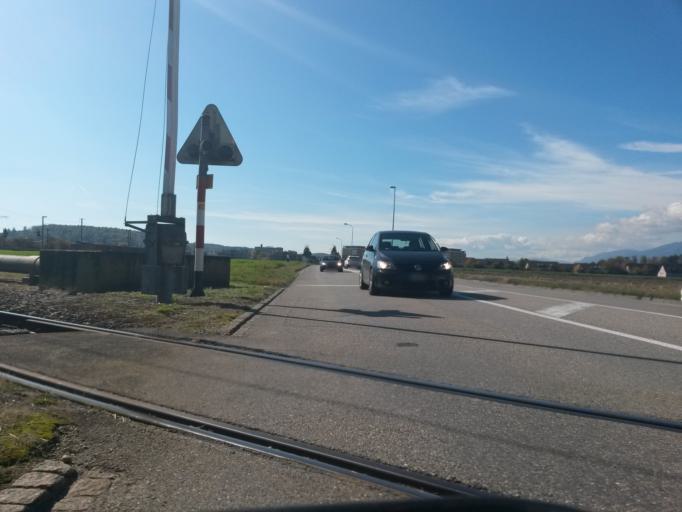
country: CH
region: Solothurn
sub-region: Bezirk Wasseramt
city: Zuchwil
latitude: 47.2130
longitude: 7.5702
